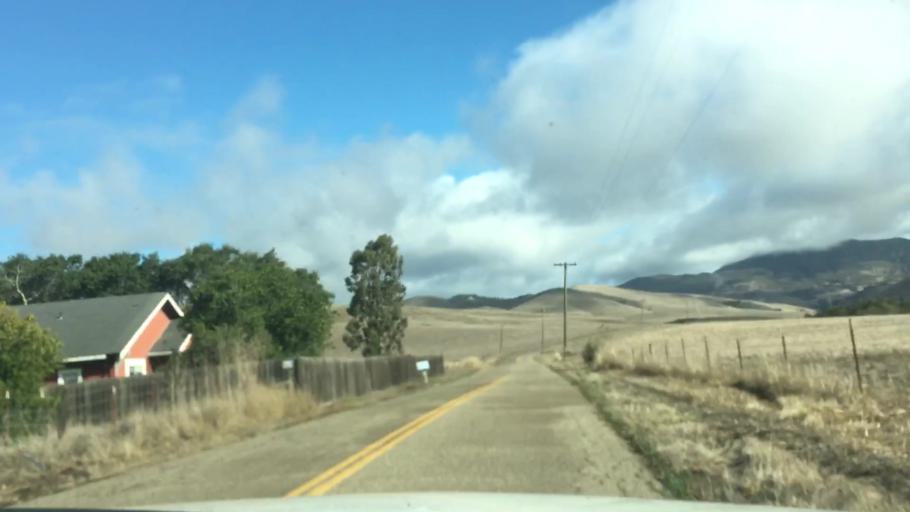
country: US
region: California
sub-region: San Luis Obispo County
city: Morro Bay
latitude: 35.3699
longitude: -120.8028
